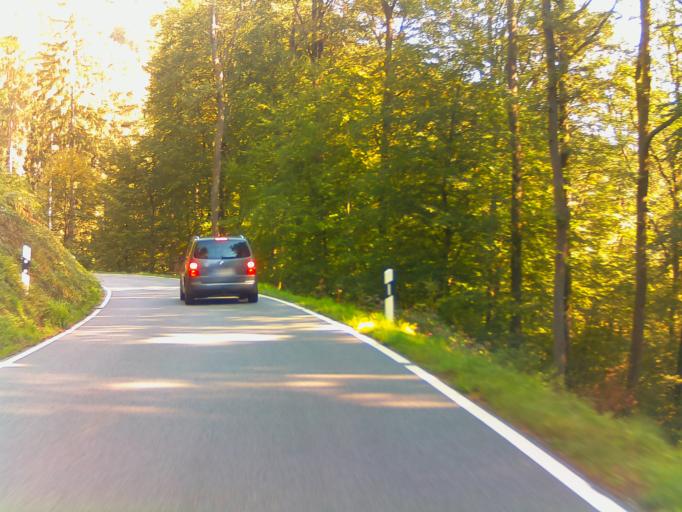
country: DE
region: Baden-Wuerttemberg
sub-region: Karlsruhe Region
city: Heddesbach
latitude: 49.4937
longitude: 8.8271
